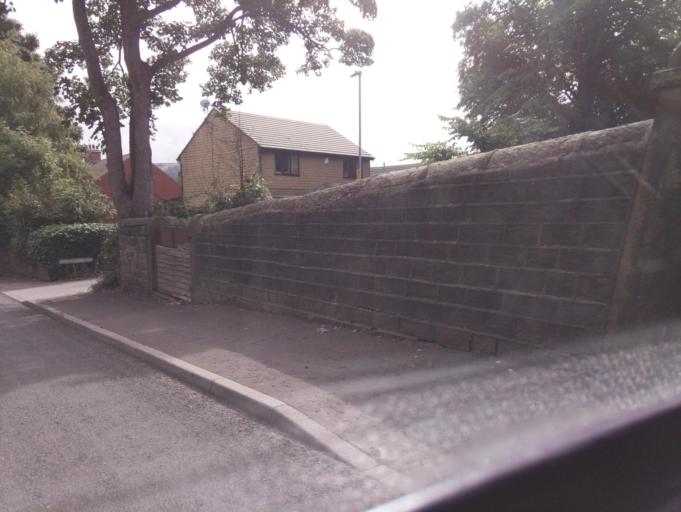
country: GB
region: England
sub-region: Kirklees
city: Holmfirth
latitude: 53.5788
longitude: -1.7605
